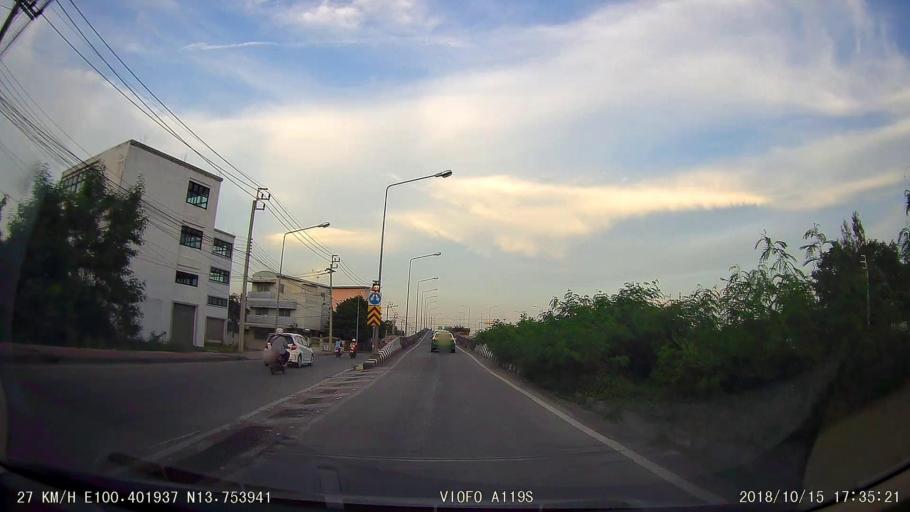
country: TH
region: Bangkok
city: Phasi Charoen
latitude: 13.7540
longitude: 100.4021
